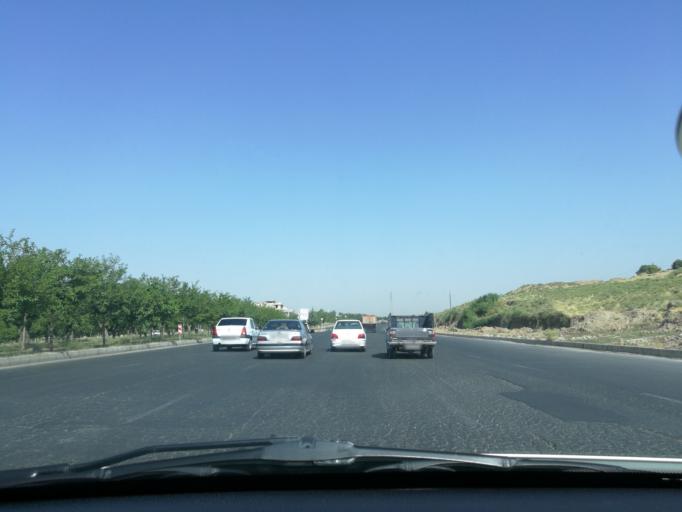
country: IR
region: Alborz
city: Karaj
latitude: 35.8635
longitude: 50.9328
